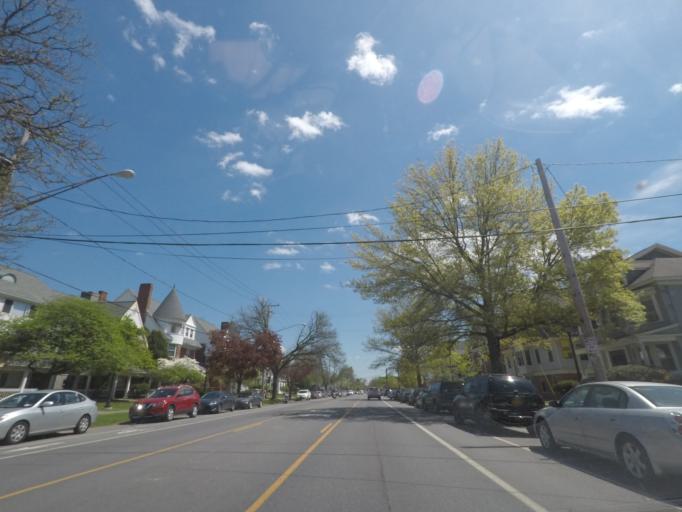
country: US
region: New York
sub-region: Albany County
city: West Albany
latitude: 42.6627
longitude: -73.7857
